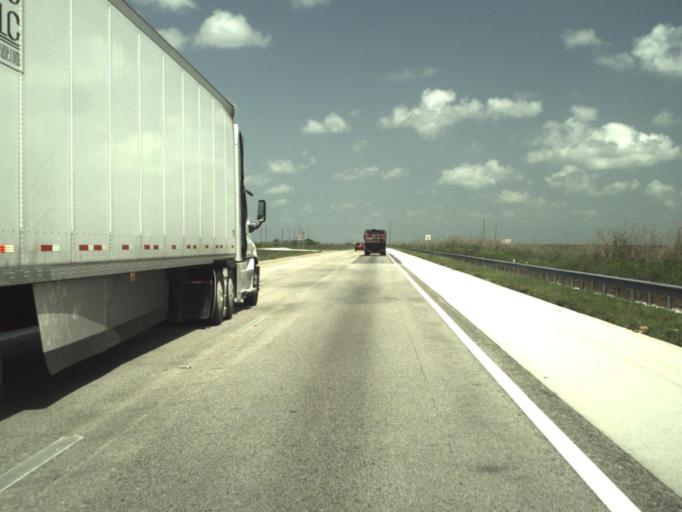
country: US
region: Florida
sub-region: Broward County
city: Coral Springs
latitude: 26.3584
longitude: -80.5558
